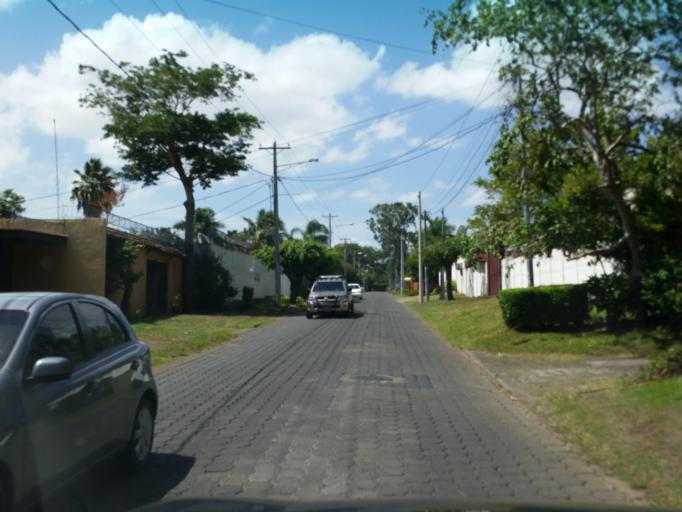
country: NI
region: Managua
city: Managua
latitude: 12.0983
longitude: -86.2338
